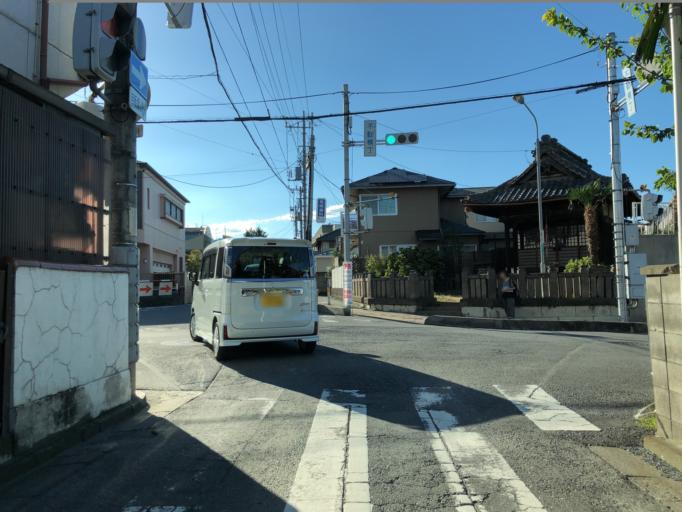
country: JP
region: Saitama
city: Fukiage-fujimi
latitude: 36.0417
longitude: 139.4029
